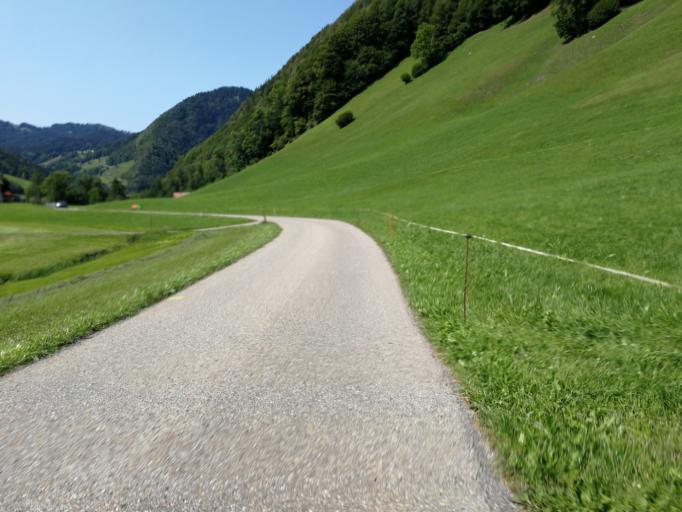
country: CH
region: Saint Gallen
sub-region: Wahlkreis Sarganserland
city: Walenstadt
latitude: 47.1905
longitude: 9.2706
